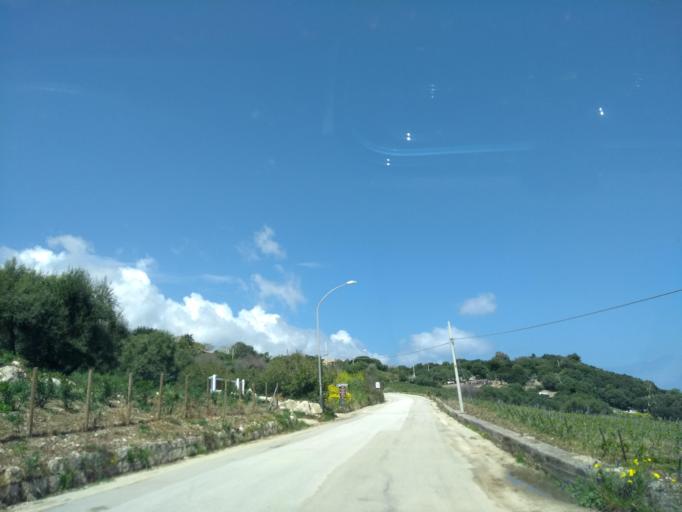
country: IT
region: Sicily
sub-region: Trapani
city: Castellammare del Golfo
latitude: 38.0661
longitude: 12.8191
